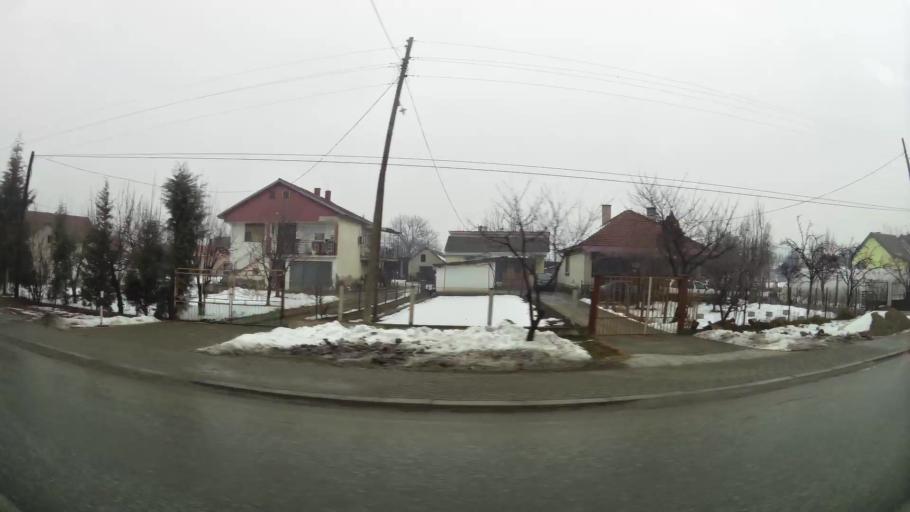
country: MK
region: Petrovec
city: Petrovec
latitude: 41.9301
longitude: 21.6258
